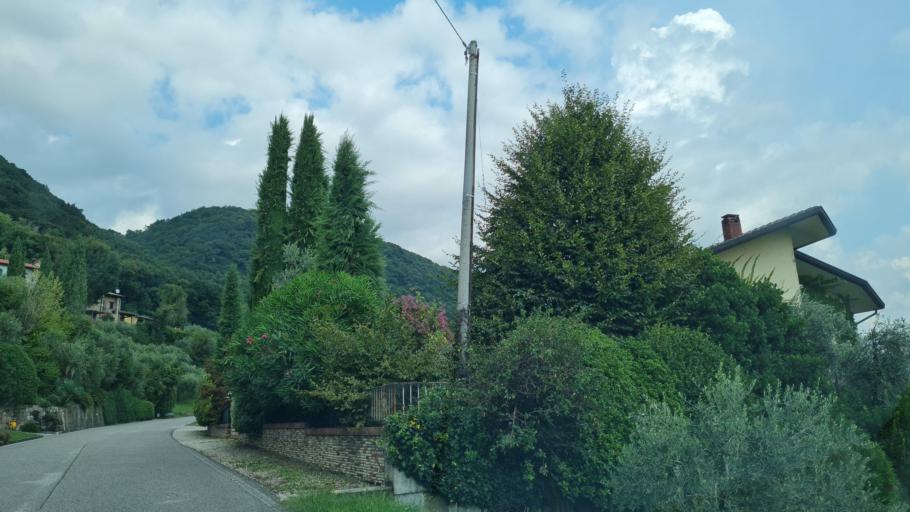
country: IT
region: Veneto
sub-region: Provincia di Vicenza
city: Marostica
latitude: 45.7766
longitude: 11.6652
